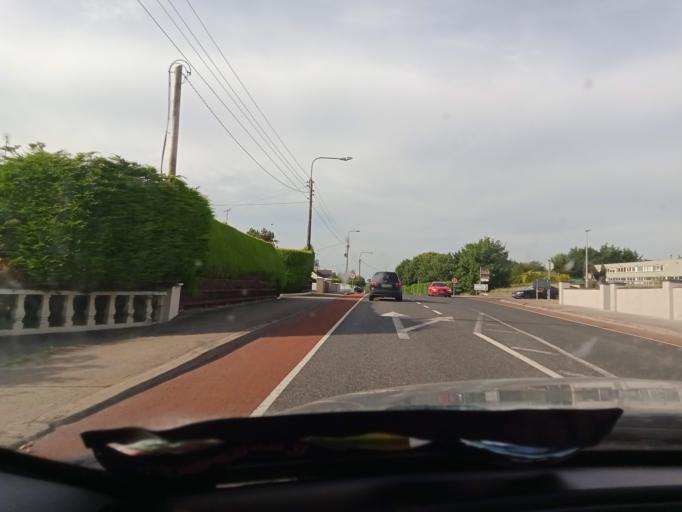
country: IE
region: Ulster
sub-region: An Cabhan
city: Cavan
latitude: 53.9698
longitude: -7.3564
